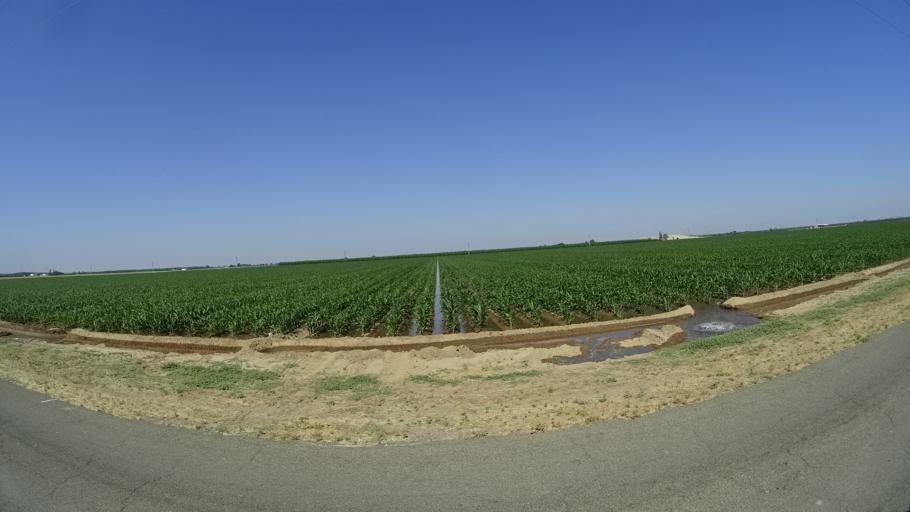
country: US
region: California
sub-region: Kings County
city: Lucerne
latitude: 36.3966
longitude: -119.5830
